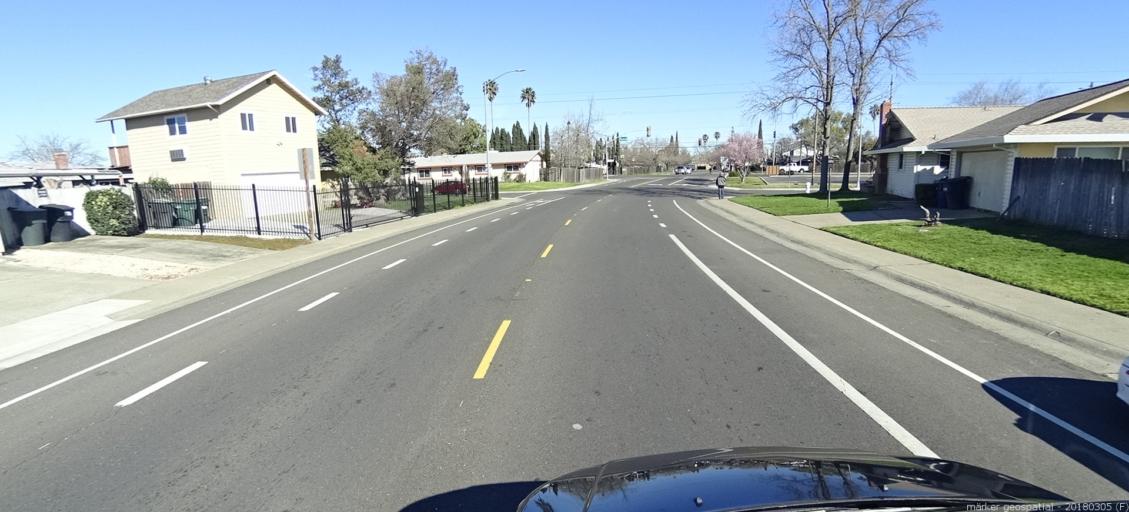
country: US
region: California
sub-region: Sacramento County
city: Florin
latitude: 38.4951
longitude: -121.4163
